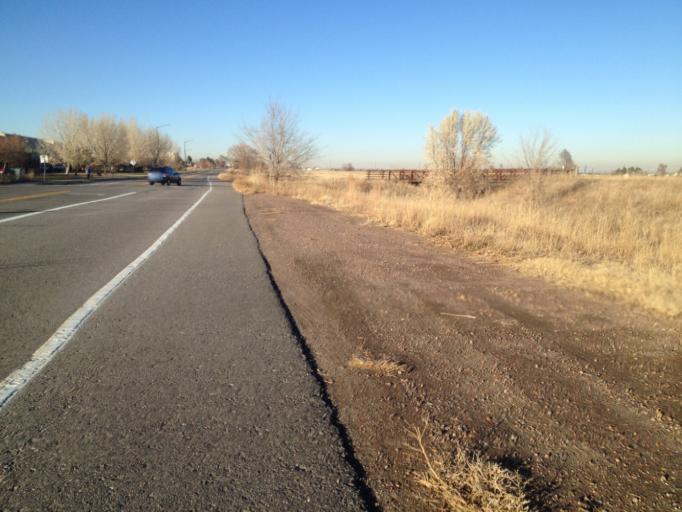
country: US
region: Colorado
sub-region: Boulder County
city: Louisville
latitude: 39.9647
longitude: -105.1093
